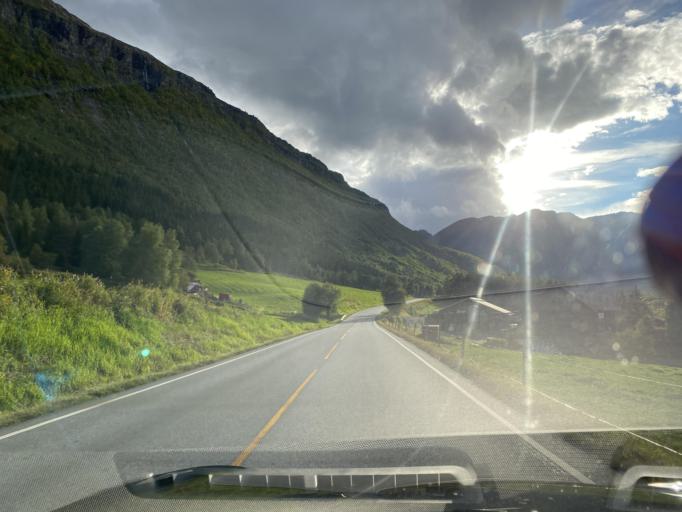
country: NO
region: Oppland
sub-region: Lom
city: Fossbergom
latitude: 61.8139
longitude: 8.5039
